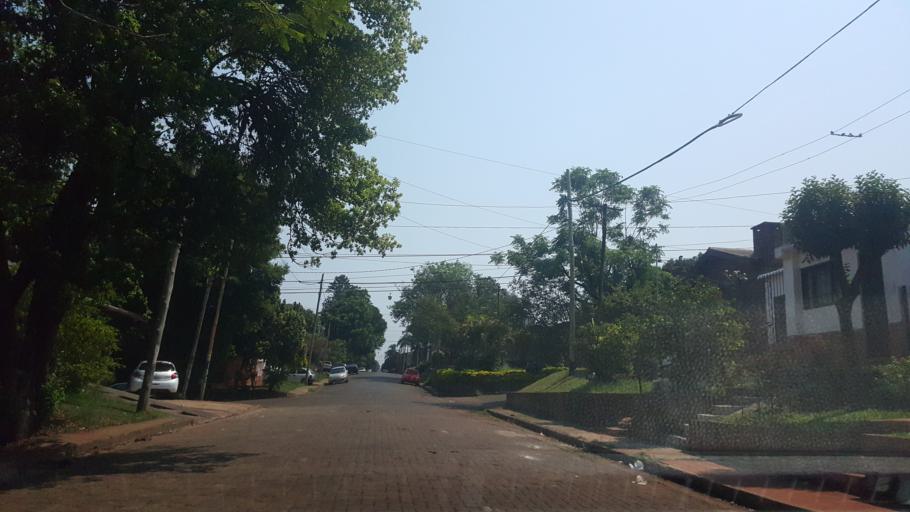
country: AR
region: Misiones
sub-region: Departamento de Capital
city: Posadas
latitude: -27.4014
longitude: -55.9075
